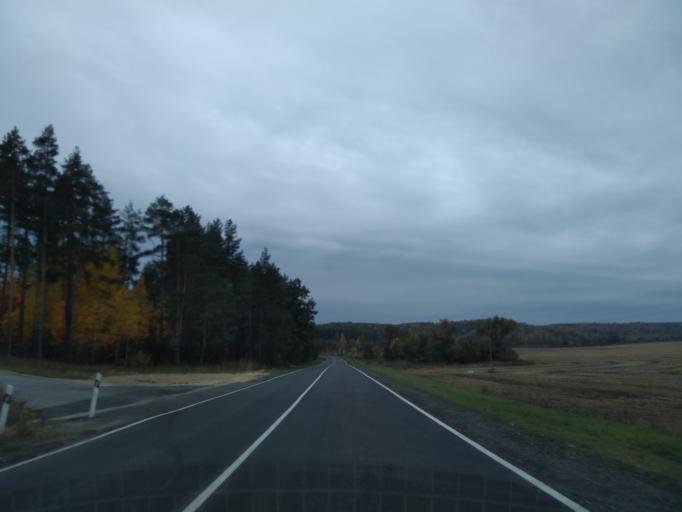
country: RU
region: Lipetsk
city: Zadonsk
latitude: 52.3587
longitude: 38.9130
